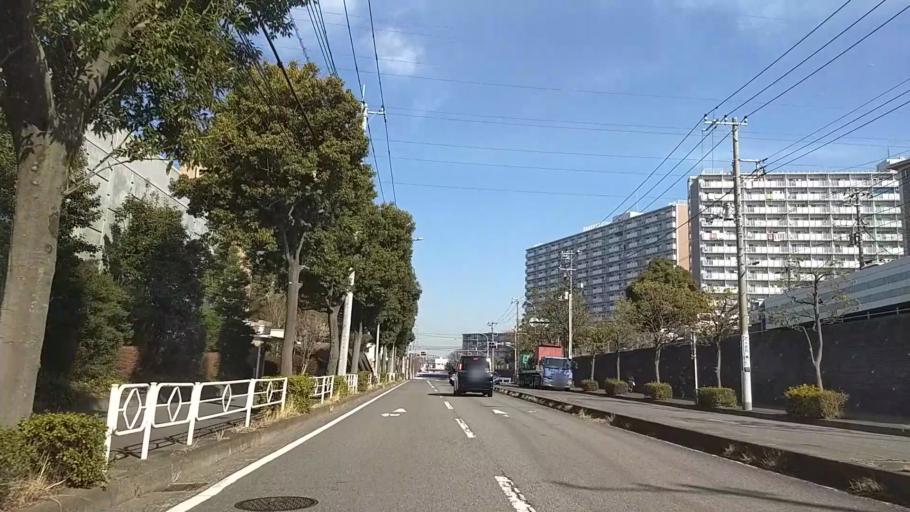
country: JP
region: Kanagawa
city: Kamakura
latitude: 35.3725
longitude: 139.5824
